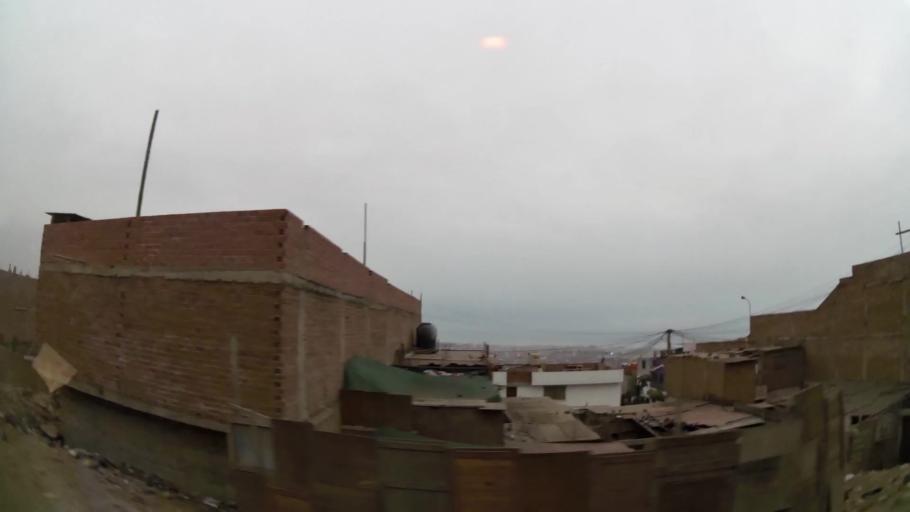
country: PE
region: Lima
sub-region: Lima
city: Surco
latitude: -12.1924
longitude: -77.0228
